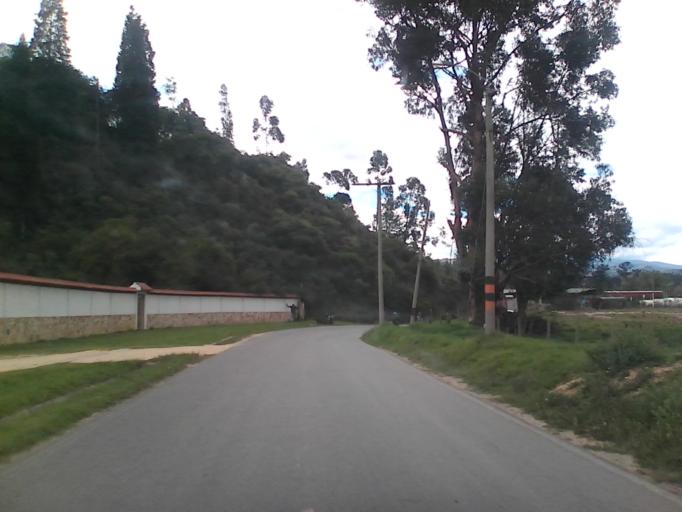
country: CO
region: Boyaca
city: Duitama
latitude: 5.7920
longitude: -73.0598
